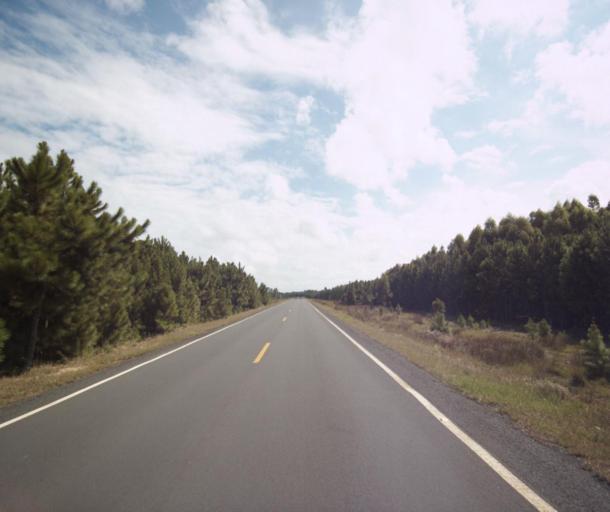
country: BR
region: Rio Grande do Sul
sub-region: Sao Lourenco Do Sul
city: Sao Lourenco do Sul
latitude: -31.4603
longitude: -51.2265
